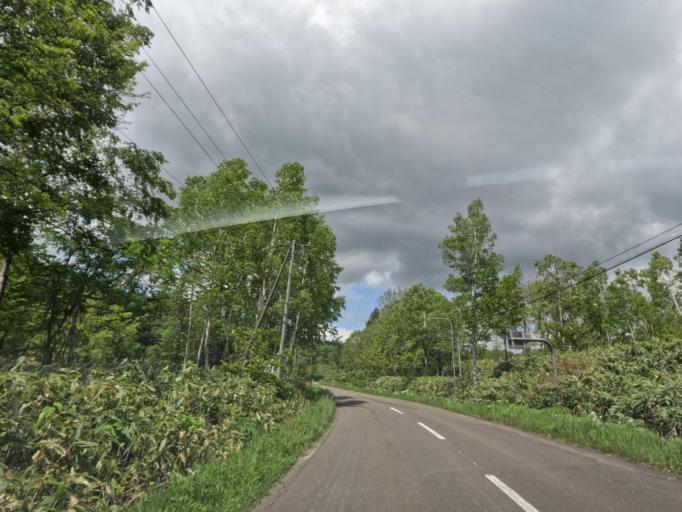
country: JP
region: Hokkaido
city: Tobetsu
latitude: 43.4434
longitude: 141.5840
